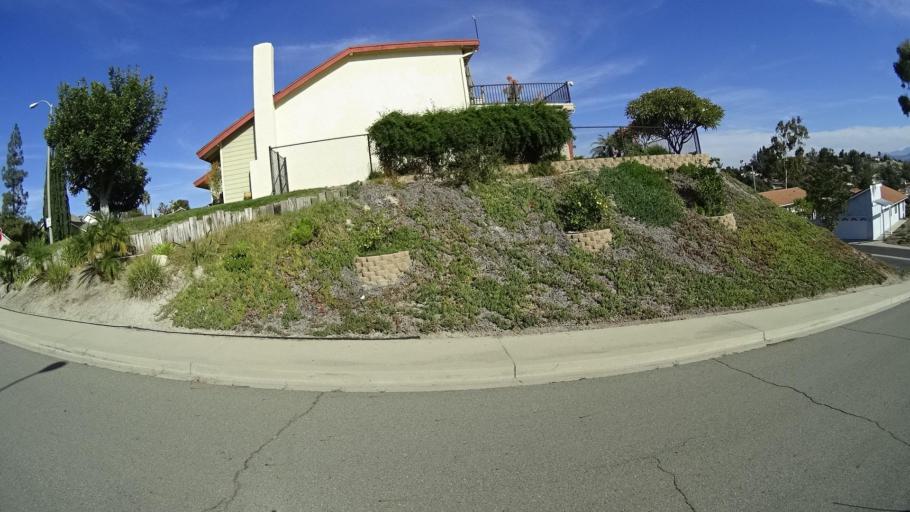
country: US
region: California
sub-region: San Diego County
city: Spring Valley
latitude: 32.7327
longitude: -116.9820
